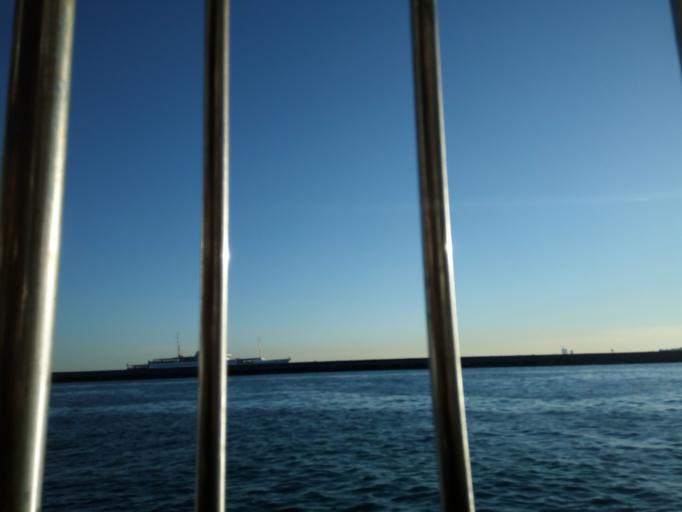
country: TR
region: Istanbul
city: UEskuedar
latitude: 41.0040
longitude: 29.0077
